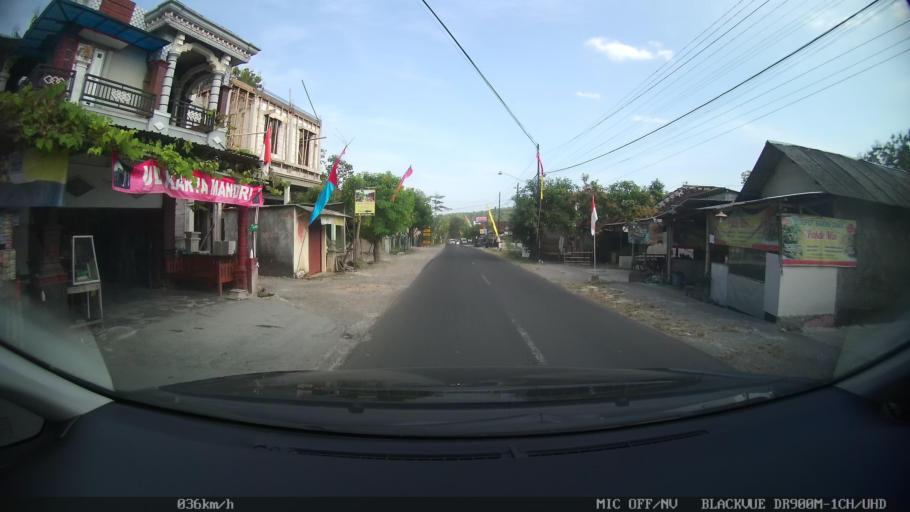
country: ID
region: Daerah Istimewa Yogyakarta
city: Kasihan
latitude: -7.8427
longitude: 110.3141
